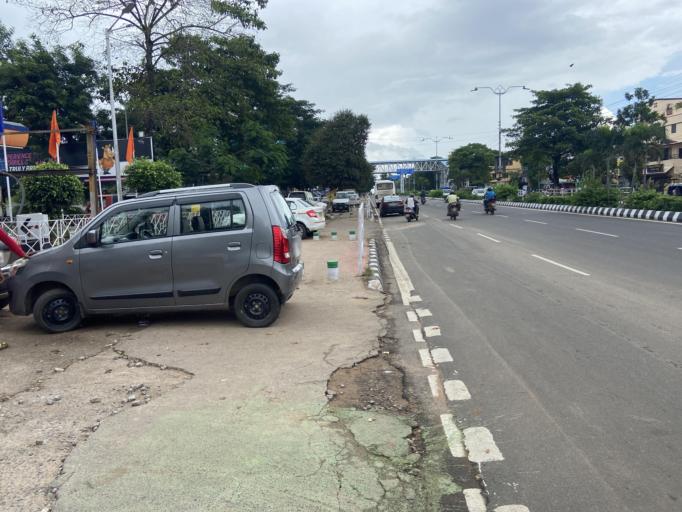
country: IN
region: Odisha
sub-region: Khordha
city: Bhubaneshwar
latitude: 20.2859
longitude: 85.8265
